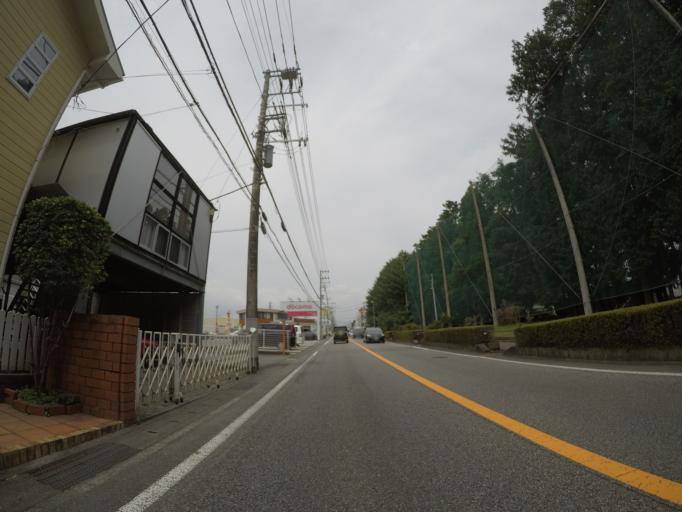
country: JP
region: Shizuoka
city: Fujinomiya
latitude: 35.2383
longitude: 138.6096
